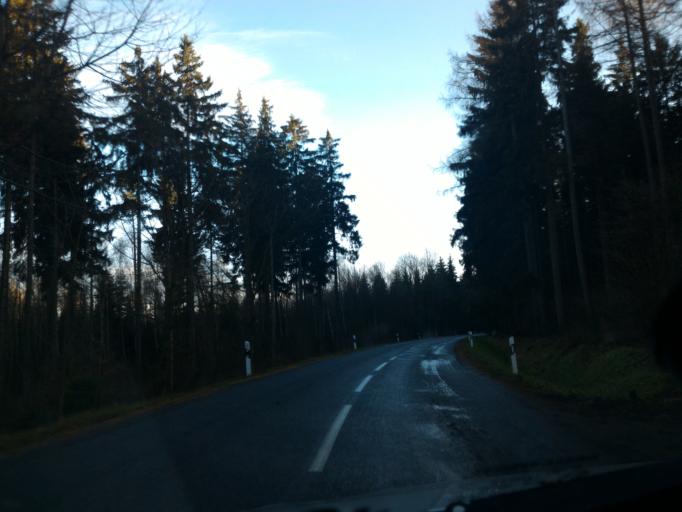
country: DE
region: Saxony
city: Kurort Jonsdorf
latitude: 50.8641
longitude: 14.6786
